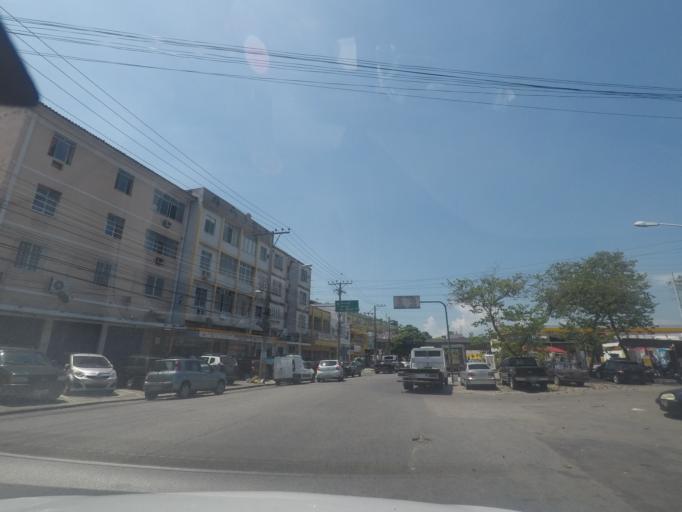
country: BR
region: Rio de Janeiro
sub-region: Rio De Janeiro
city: Rio de Janeiro
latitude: -22.8727
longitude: -43.2584
